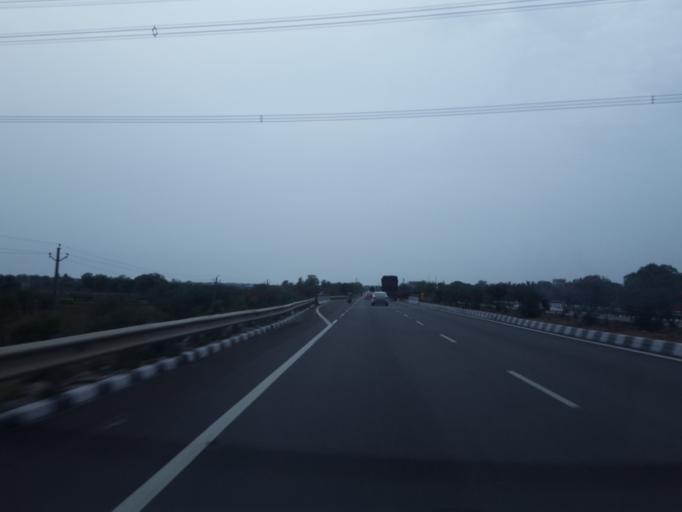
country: IN
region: Telangana
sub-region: Mahbubnagar
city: Farrukhnagar
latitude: 17.0822
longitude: 78.2318
